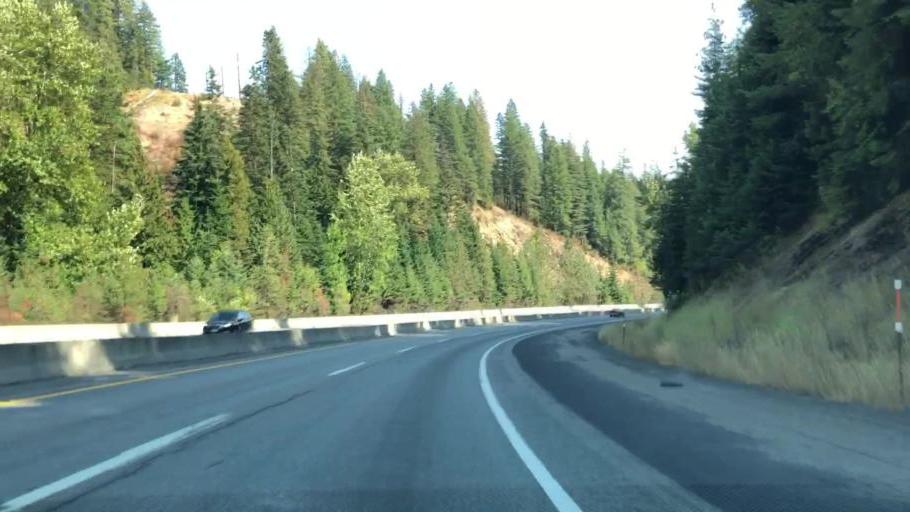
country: US
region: Idaho
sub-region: Kootenai County
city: Coeur d'Alene
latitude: 47.6101
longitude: -116.5142
